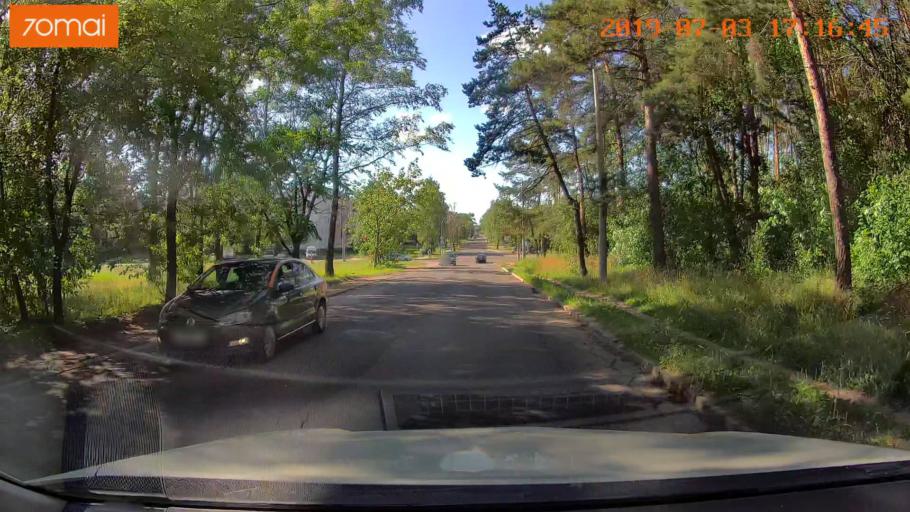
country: BY
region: Minsk
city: Vyaliki Trastsyanets
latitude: 53.9081
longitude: 27.6751
